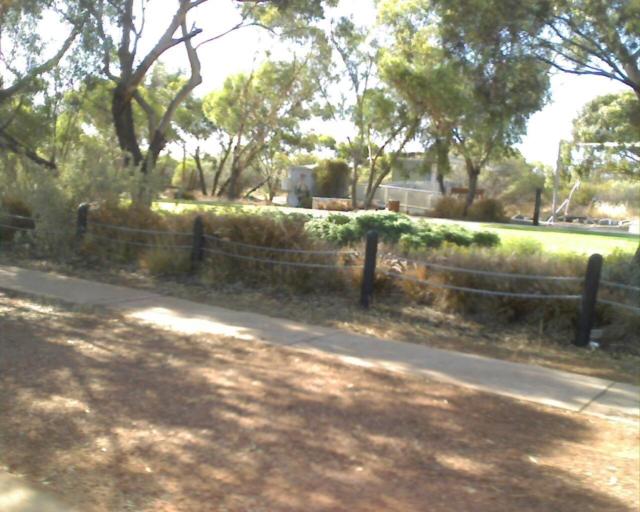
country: AU
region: Western Australia
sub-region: Wongan-Ballidu
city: Wongan Hills
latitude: -30.2800
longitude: 116.6583
